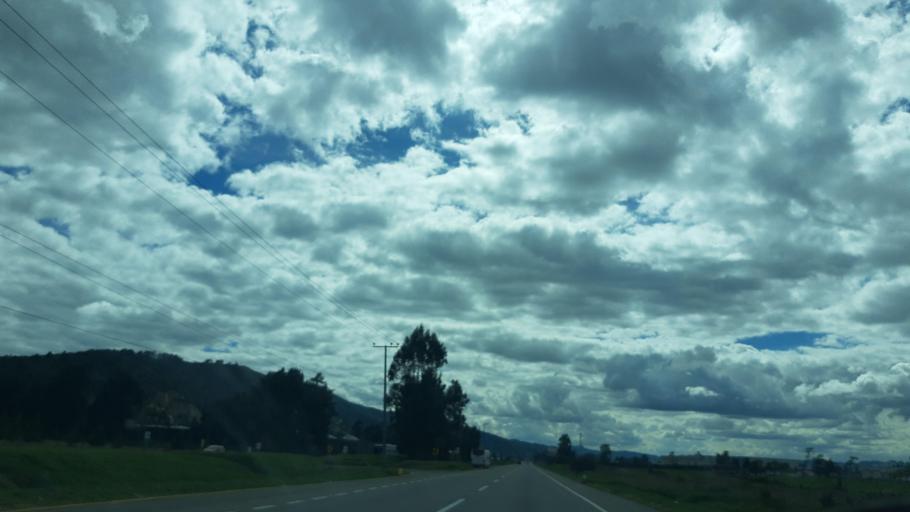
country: CO
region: Cundinamarca
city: Gachancipa
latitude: 5.0167
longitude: -73.8524
